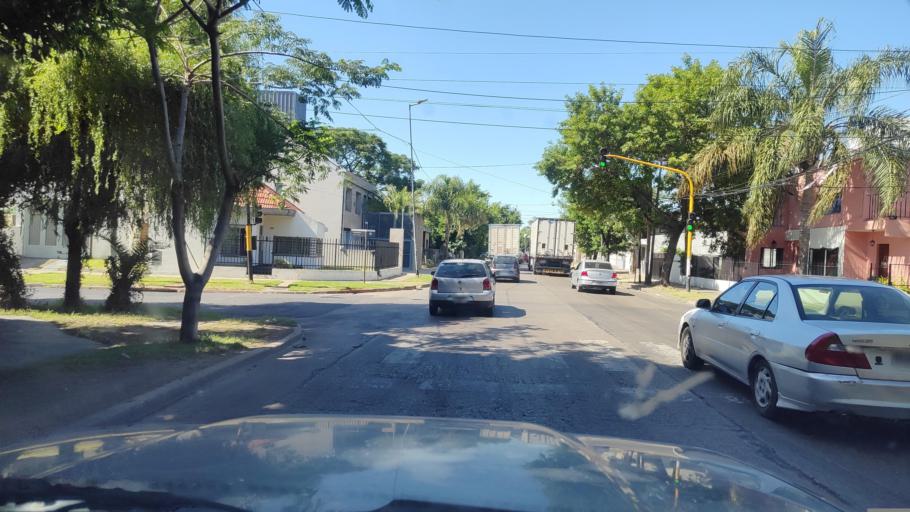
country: AR
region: Buenos Aires
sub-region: Partido de Moron
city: Moron
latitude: -34.6544
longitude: -58.6311
